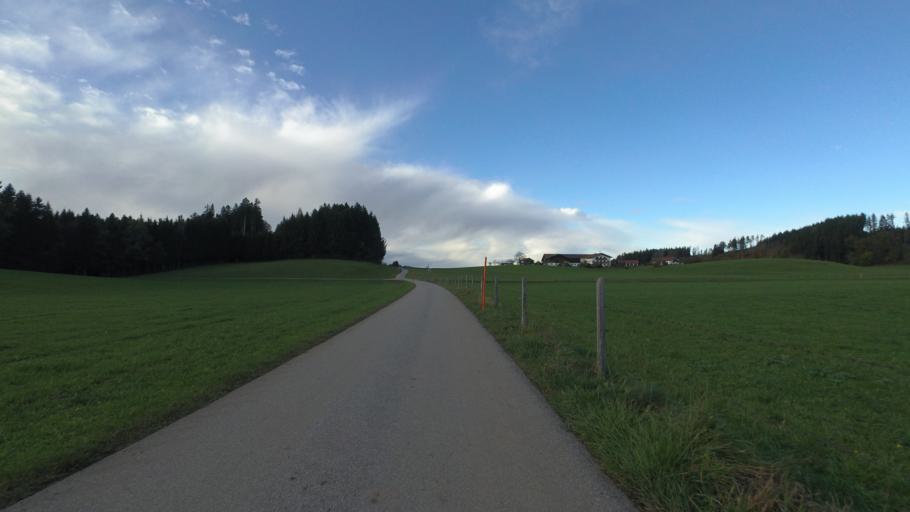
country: DE
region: Bavaria
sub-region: Upper Bavaria
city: Nussdorf
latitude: 47.9287
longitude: 12.5687
